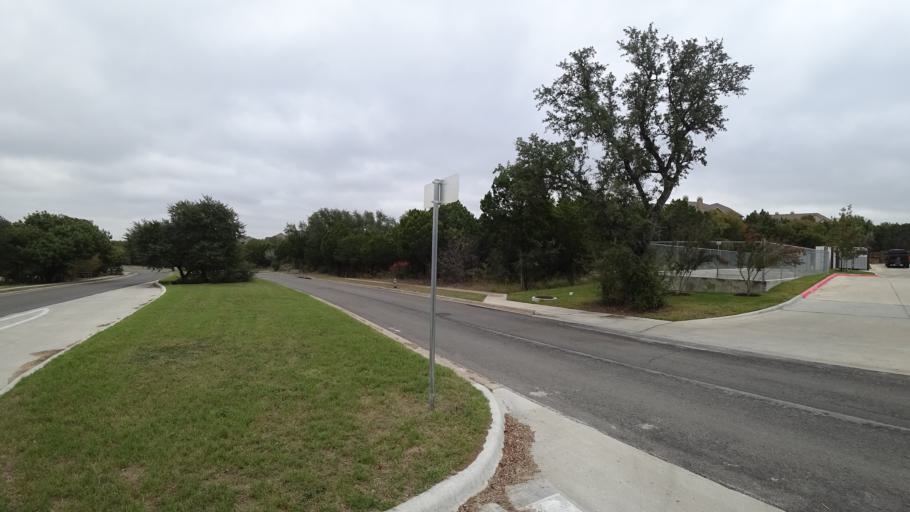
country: US
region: Texas
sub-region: Williamson County
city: Anderson Mill
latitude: 30.4285
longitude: -97.8418
